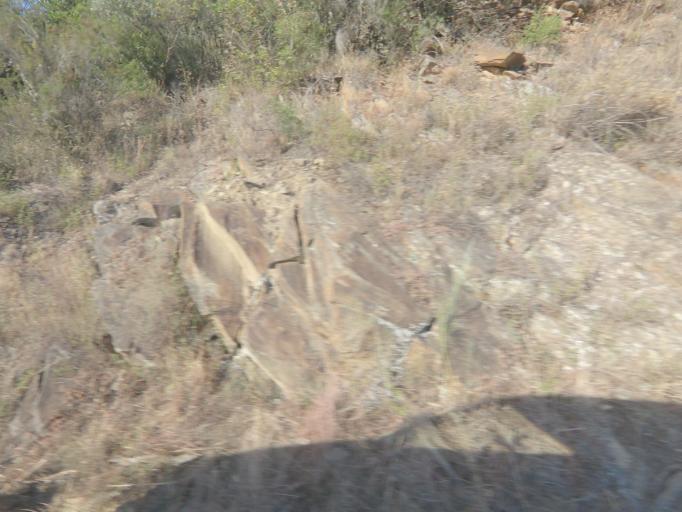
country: PT
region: Vila Real
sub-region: Sabrosa
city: Sabrosa
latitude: 41.2677
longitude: -7.5476
